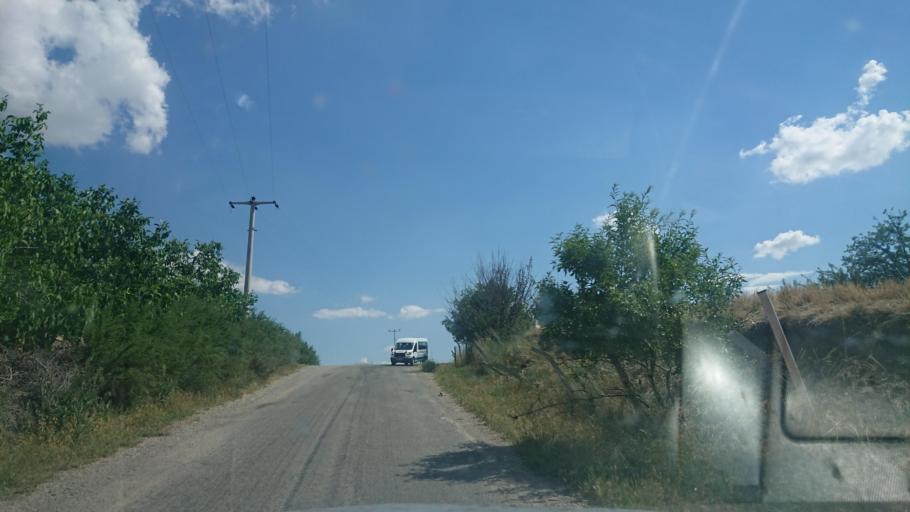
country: TR
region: Aksaray
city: Agacoren
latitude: 38.7663
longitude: 33.7841
